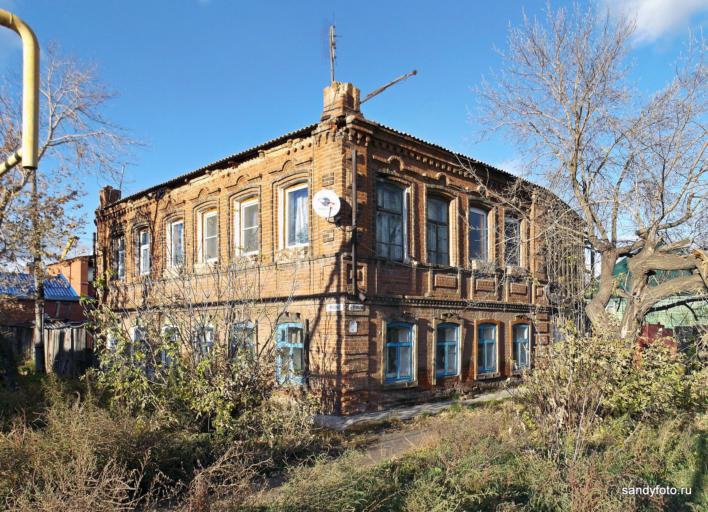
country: RU
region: Chelyabinsk
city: Troitsk
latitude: 54.0760
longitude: 61.5427
